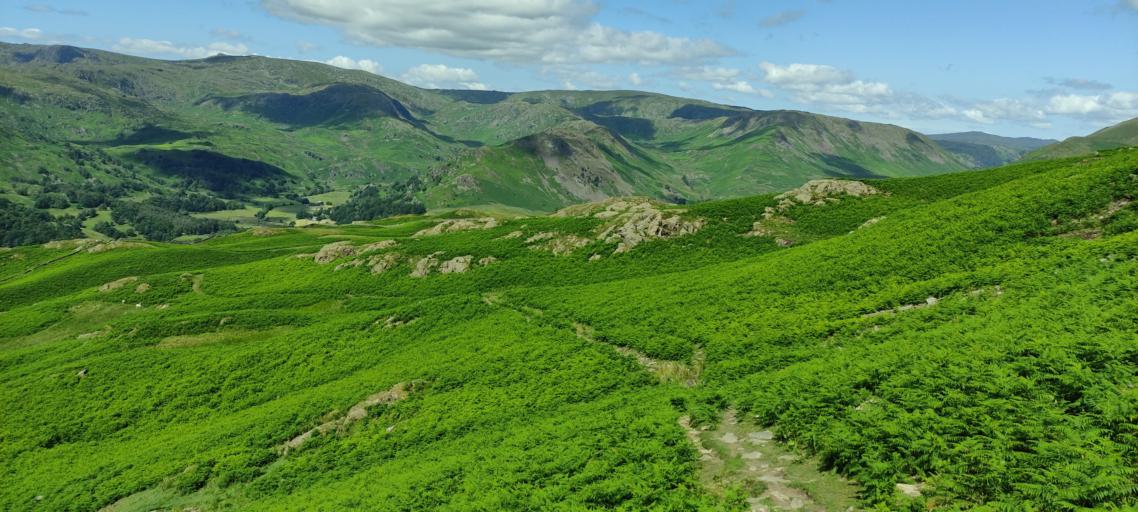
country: GB
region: England
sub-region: Cumbria
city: Ambleside
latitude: 54.4606
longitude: -3.0009
